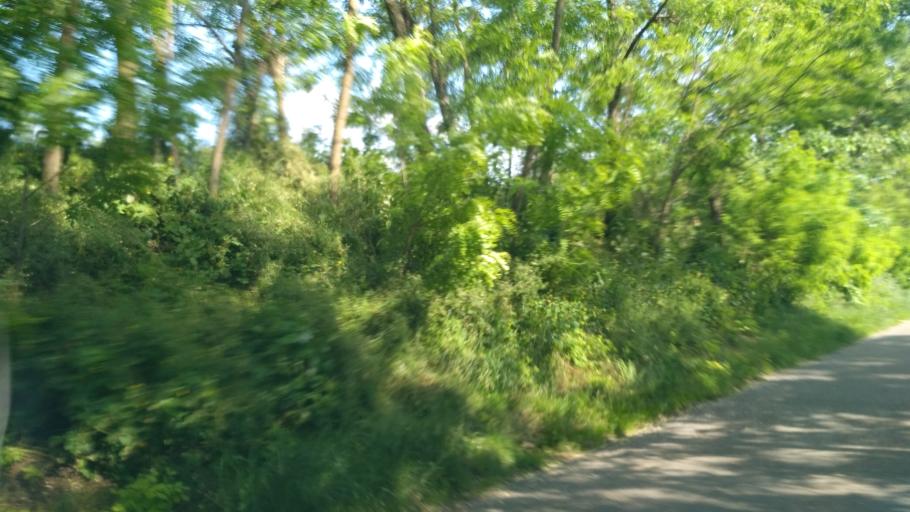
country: PL
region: Subcarpathian Voivodeship
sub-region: Powiat jaroslawski
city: Ostrow
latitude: 49.9283
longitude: 22.7403
